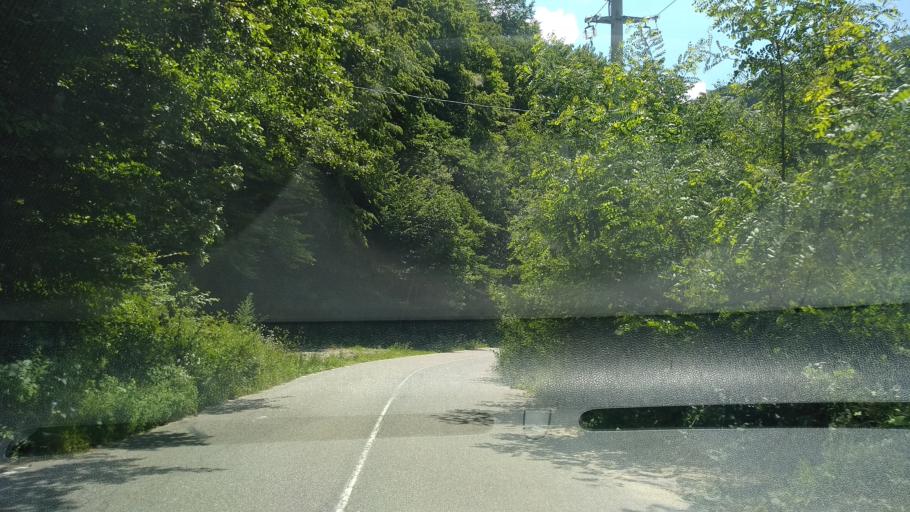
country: RO
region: Hunedoara
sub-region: Comuna Orastioara de Sus
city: Orastioara de Sus
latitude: 45.6696
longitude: 23.1718
